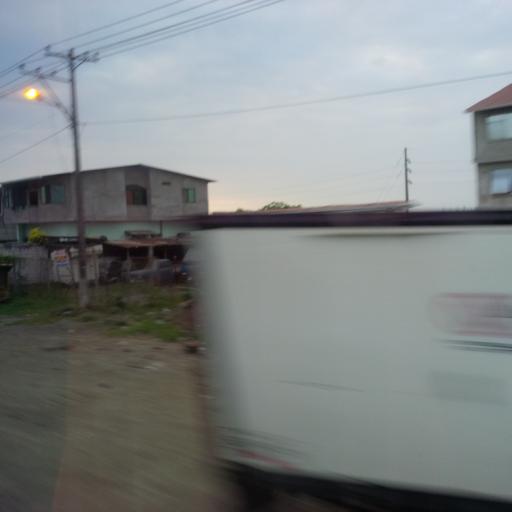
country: EC
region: Guayas
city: Coronel Marcelino Mariduena
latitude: -2.3275
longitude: -79.4136
